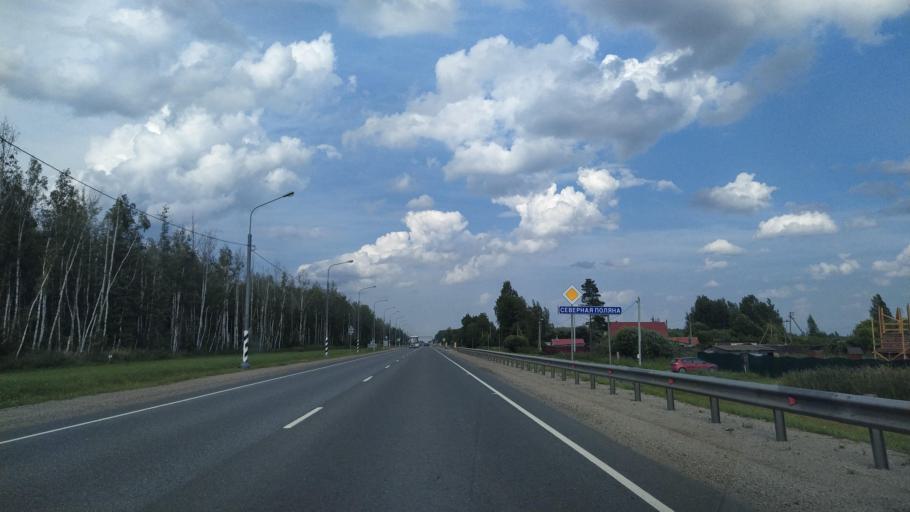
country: RU
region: Novgorod
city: Shimsk
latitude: 58.2556
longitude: 30.7991
